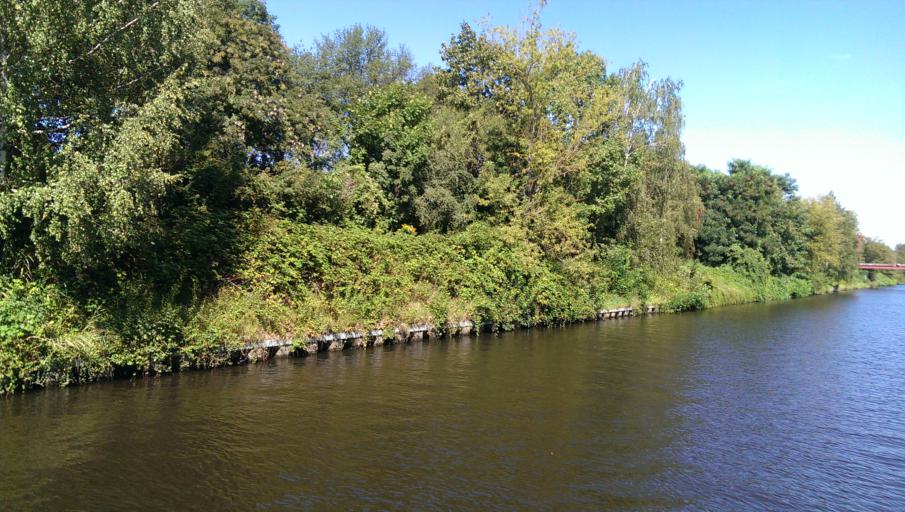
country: DE
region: Berlin
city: Lichterfelde
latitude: 52.4239
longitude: 13.3057
